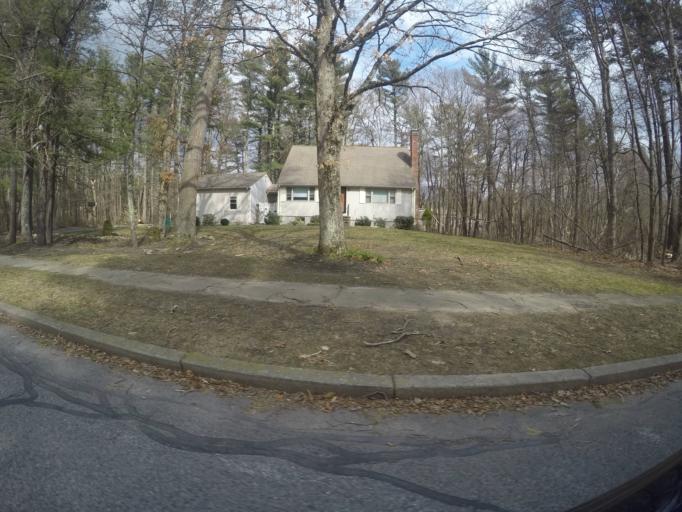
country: US
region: Massachusetts
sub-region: Bristol County
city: Easton
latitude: 42.0410
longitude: -71.1156
